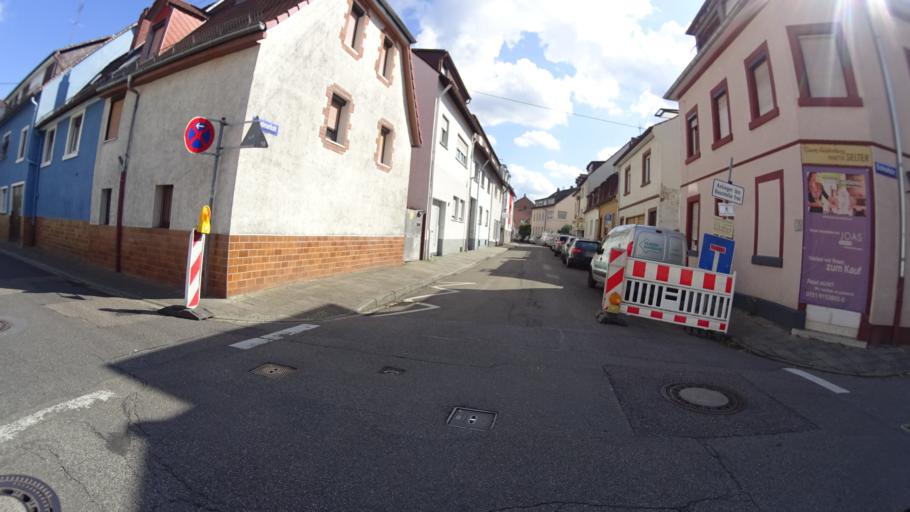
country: DE
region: Baden-Wuerttemberg
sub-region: Karlsruhe Region
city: Karlsruhe
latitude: 48.9895
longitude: 8.4580
